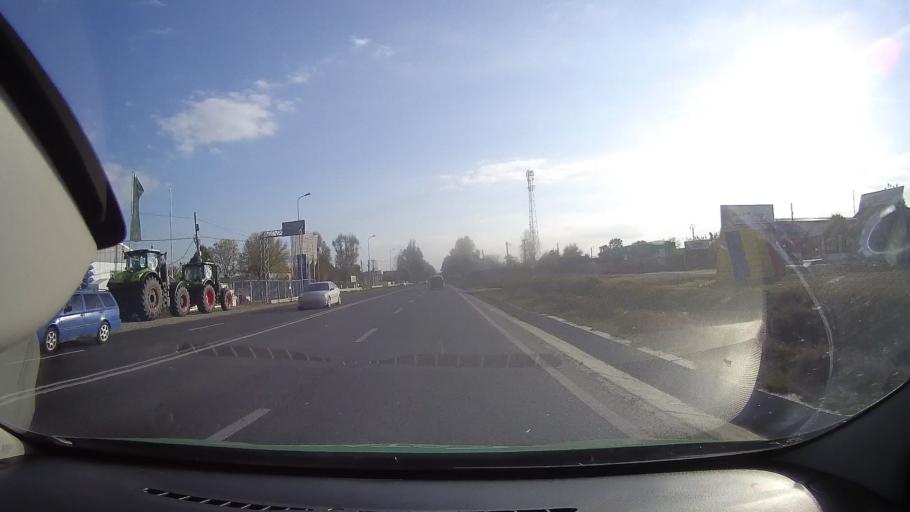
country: RO
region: Constanta
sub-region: Comuna Lumina
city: Lumina
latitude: 44.2827
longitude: 28.5569
